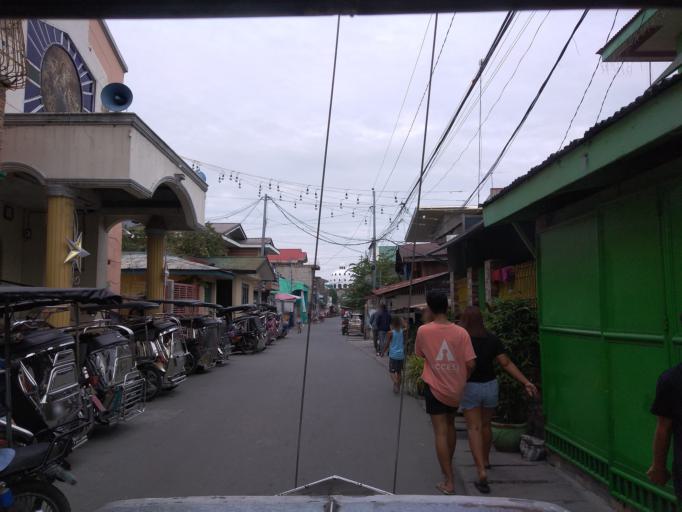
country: PH
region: Central Luzon
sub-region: Province of Pampanga
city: Sexmoan
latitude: 14.9337
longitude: 120.6249
